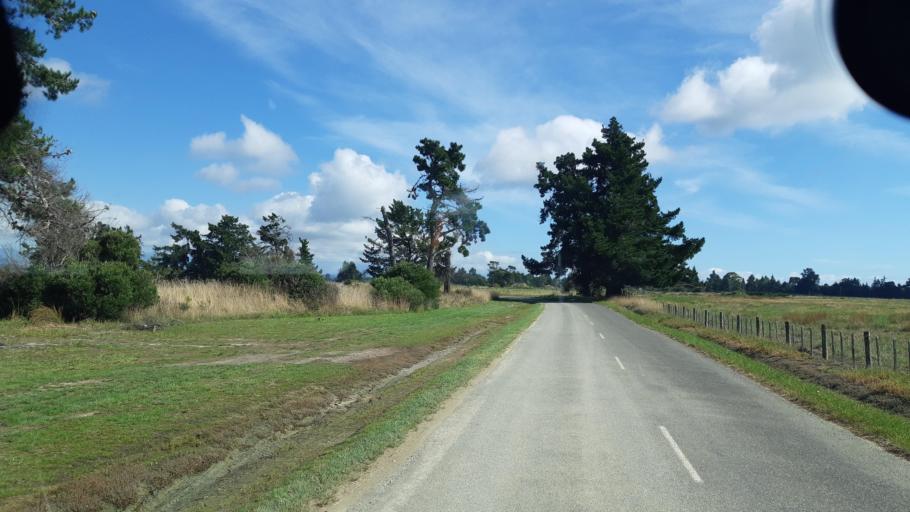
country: NZ
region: Tasman
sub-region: Tasman District
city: Richmond
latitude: -41.2996
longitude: 173.1586
